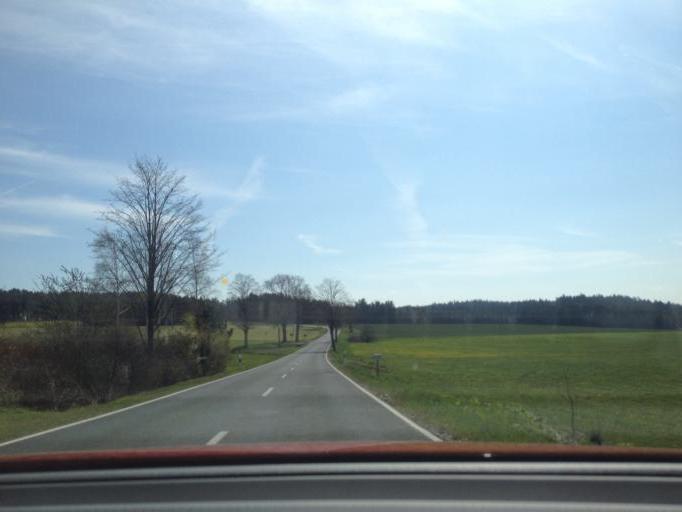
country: DE
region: Bavaria
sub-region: Upper Franconia
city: Roslau
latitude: 50.0774
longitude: 12.0155
